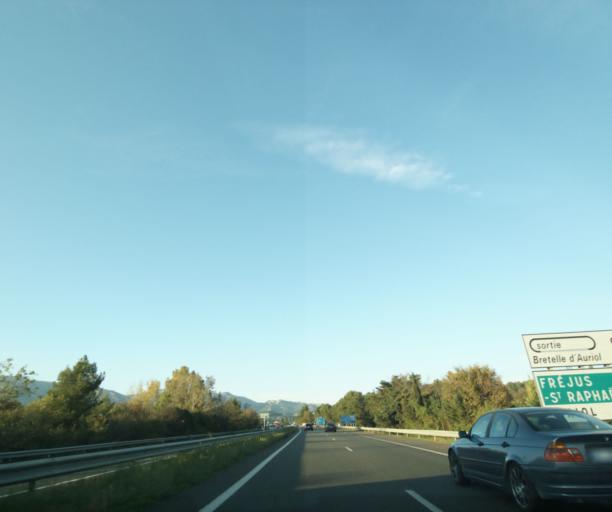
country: FR
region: Provence-Alpes-Cote d'Azur
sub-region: Departement des Bouches-du-Rhone
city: Aubagne
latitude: 43.3085
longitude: 5.5921
